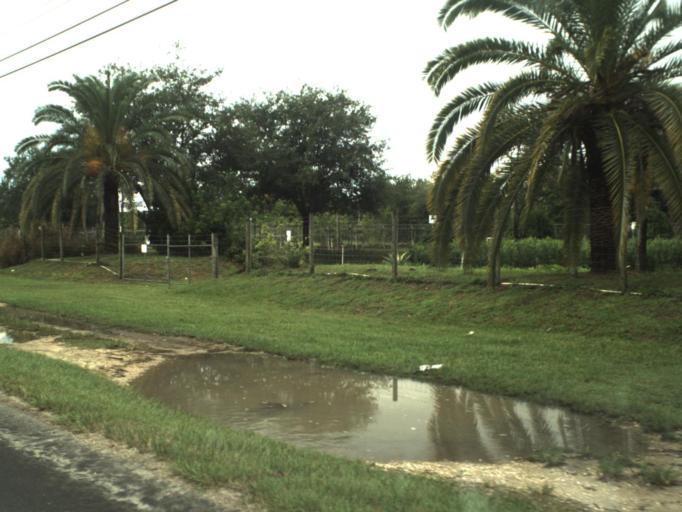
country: US
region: Florida
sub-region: Miami-Dade County
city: Richmond West
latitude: 25.5718
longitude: -80.4783
